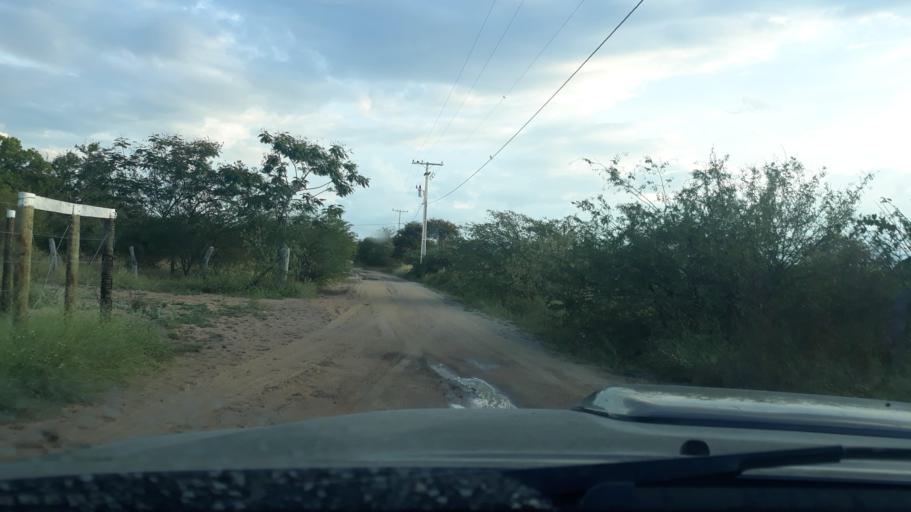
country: BR
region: Bahia
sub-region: Riacho De Santana
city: Riacho de Santana
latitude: -13.8819
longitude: -43.0211
